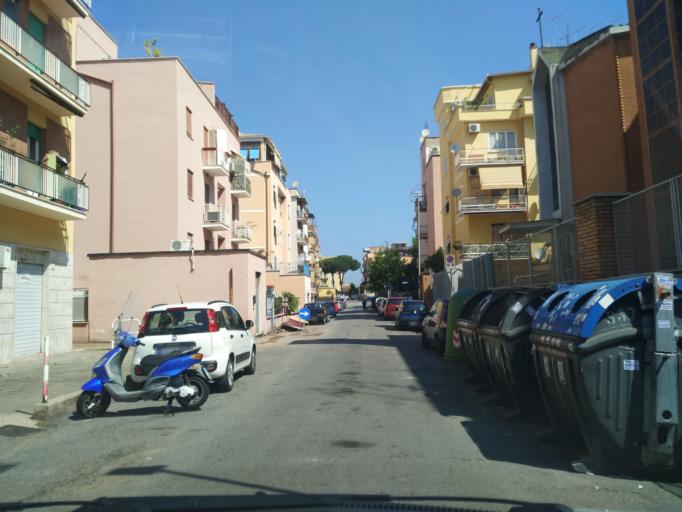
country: IT
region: Latium
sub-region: Citta metropolitana di Roma Capitale
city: Rome
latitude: 41.8759
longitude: 12.5761
